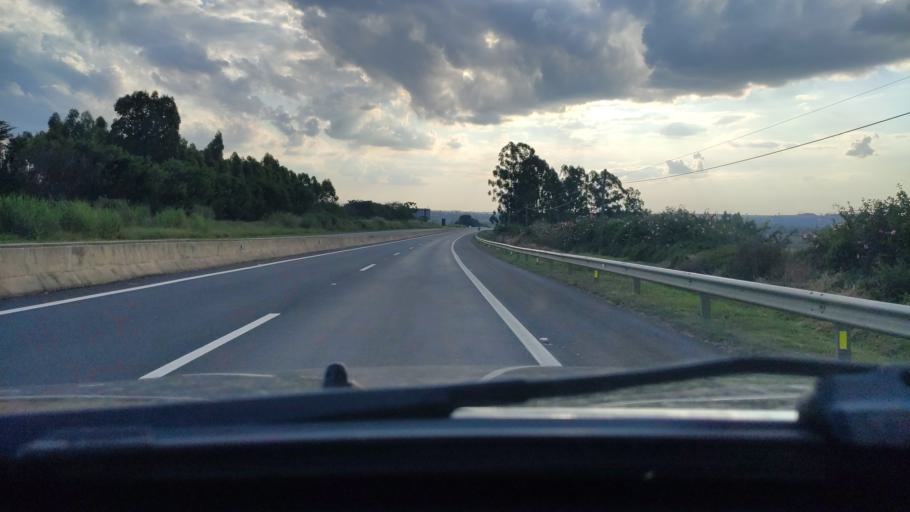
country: BR
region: Sao Paulo
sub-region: Mogi-Mirim
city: Mogi Mirim
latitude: -22.4447
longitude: -47.0267
